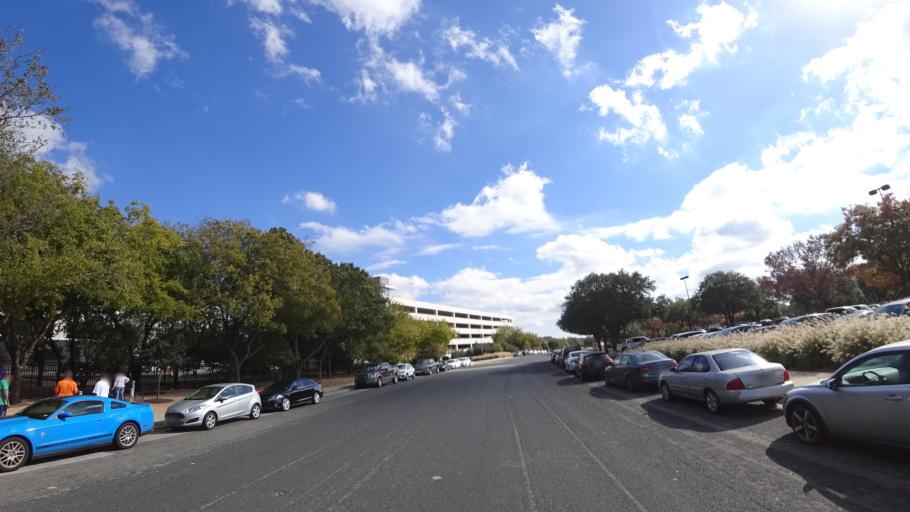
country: US
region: Texas
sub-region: Williamson County
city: Jollyville
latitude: 30.4331
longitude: -97.7351
